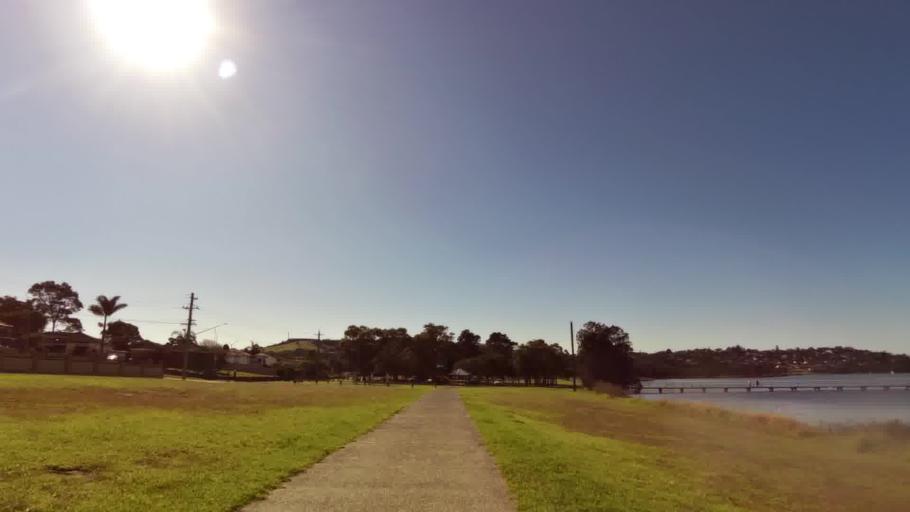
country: AU
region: New South Wales
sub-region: Wollongong
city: Berkeley
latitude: -34.4849
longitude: 150.8444
